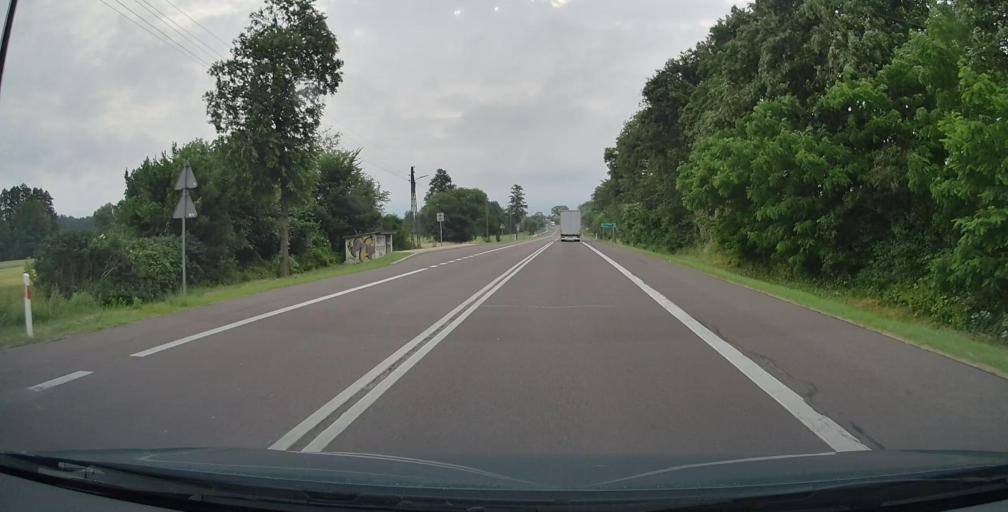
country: PL
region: Lublin Voivodeship
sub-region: Powiat bialski
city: Miedzyrzec Podlaski
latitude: 52.0280
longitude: 22.8716
